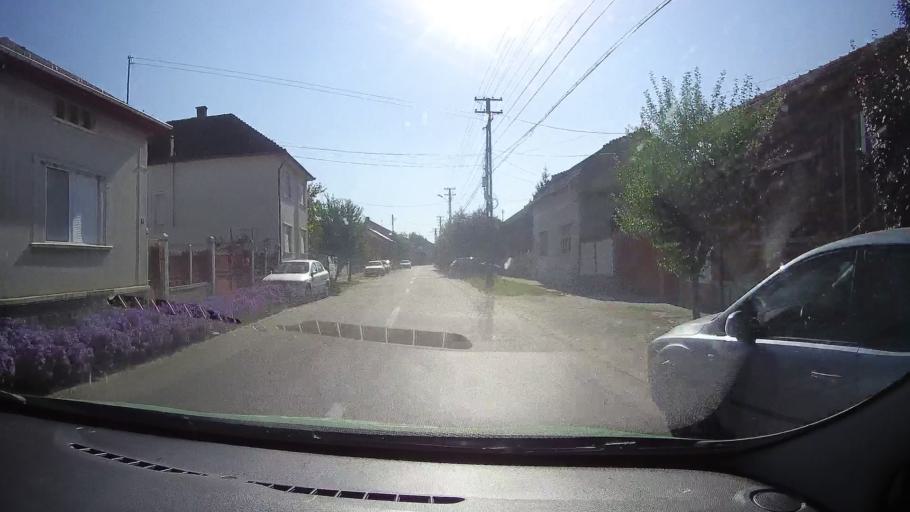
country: RO
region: Satu Mare
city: Carei
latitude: 47.6907
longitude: 22.4706
